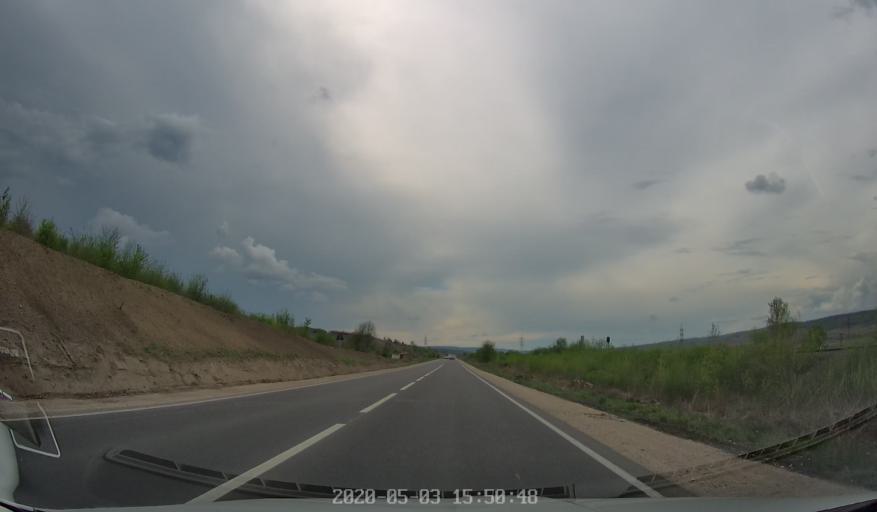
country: MD
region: Straseni
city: Straseni
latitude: 47.1600
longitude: 28.5712
